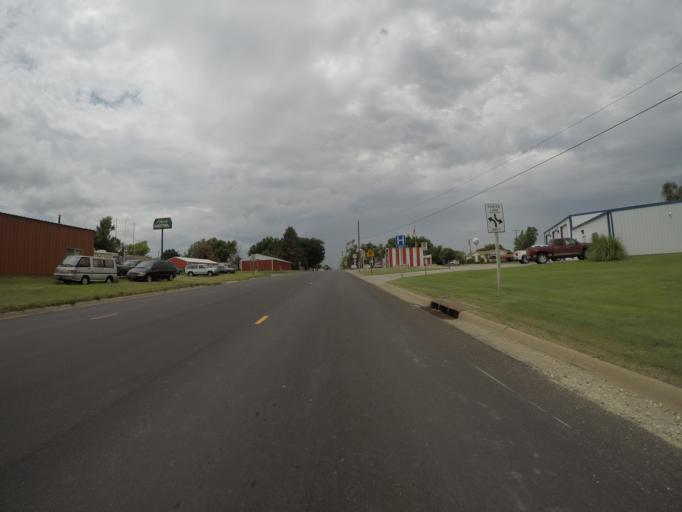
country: US
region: Kansas
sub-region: Sheridan County
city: Hoxie
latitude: 39.3578
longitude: -100.4329
